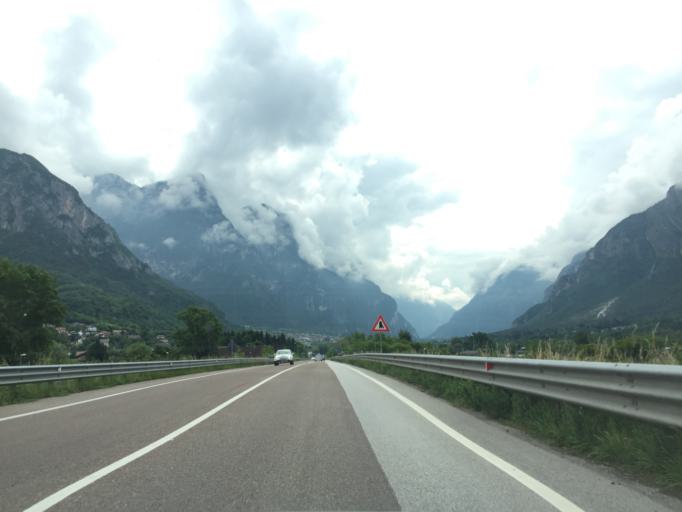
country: IT
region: Trentino-Alto Adige
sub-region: Provincia di Trento
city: Villa-Agnedo
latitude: 46.0501
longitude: 11.5207
